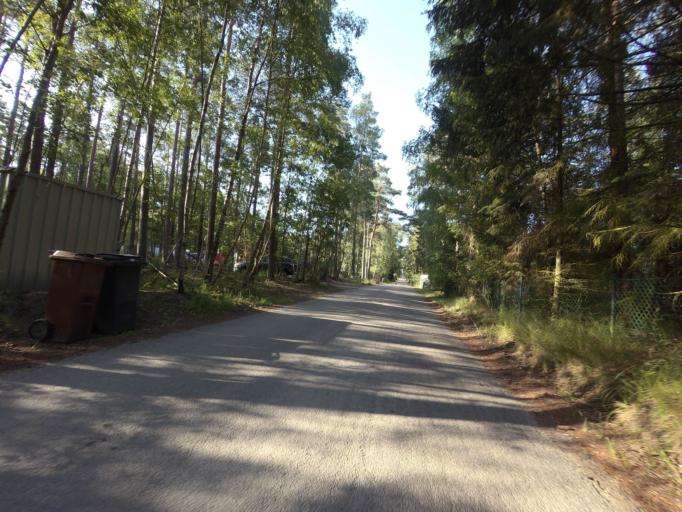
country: SE
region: Skane
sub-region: Landskrona
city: Asmundtorp
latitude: 55.8389
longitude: 12.9320
